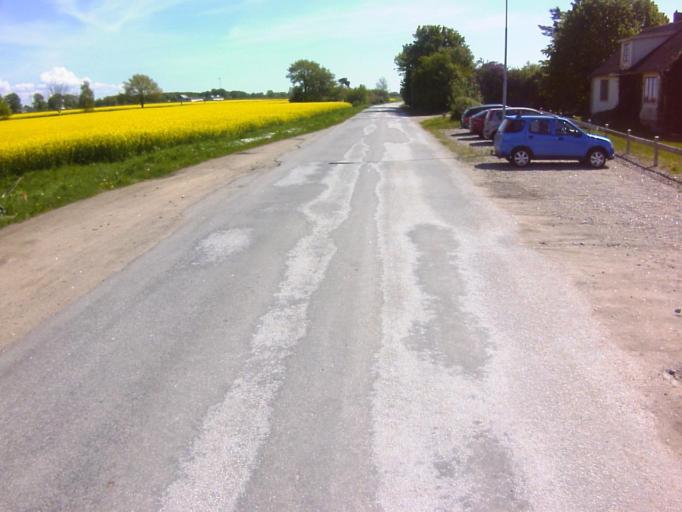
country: SE
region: Blekinge
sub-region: Solvesborgs Kommun
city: Soelvesborg
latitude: 56.0548
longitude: 14.6345
